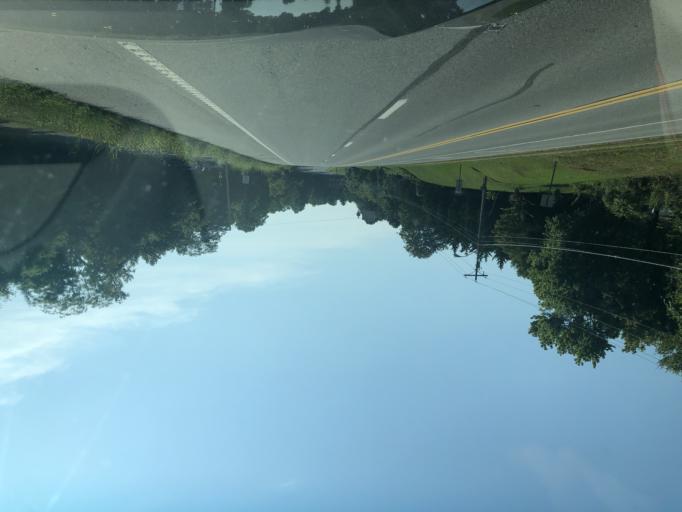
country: US
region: Tennessee
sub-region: Franklin County
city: Sewanee
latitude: 35.1951
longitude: -85.9166
